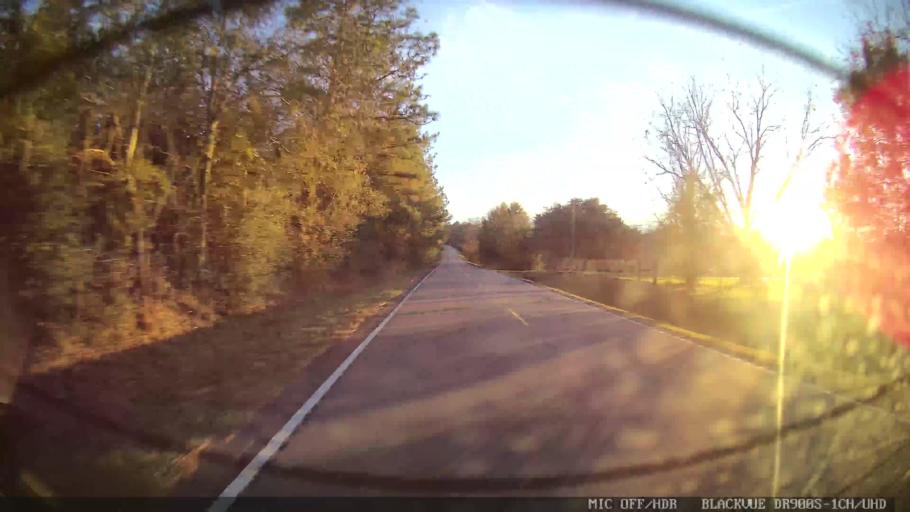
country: US
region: Mississippi
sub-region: Stone County
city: Wiggins
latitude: 31.0137
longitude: -89.2557
